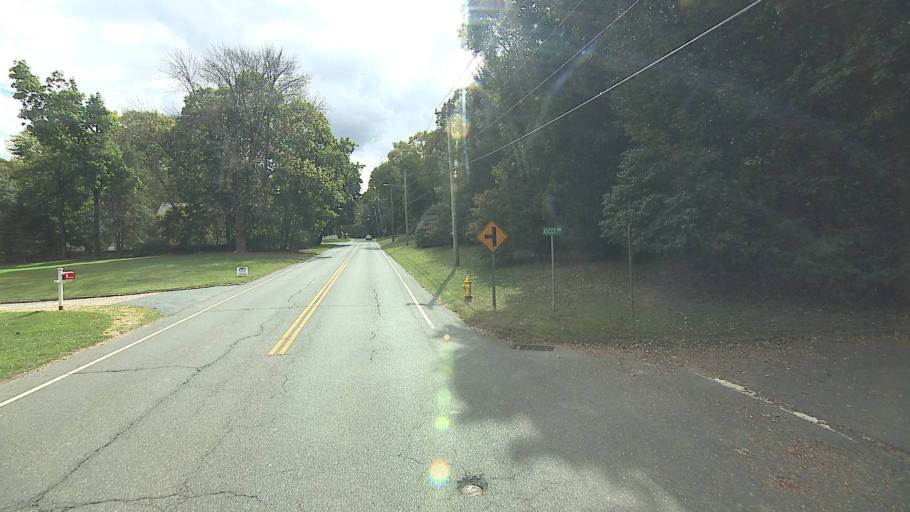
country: US
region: Connecticut
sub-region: Fairfield County
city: Ridgefield
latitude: 41.2677
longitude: -73.4954
